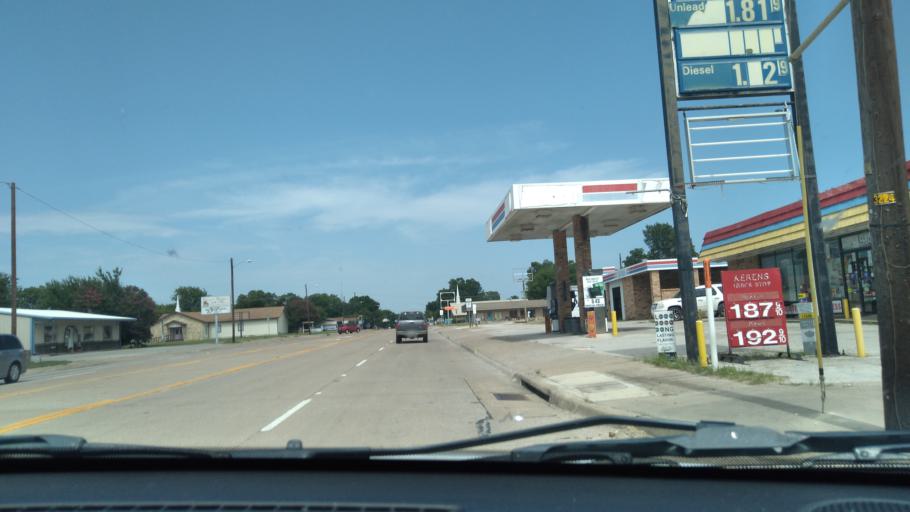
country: US
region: Texas
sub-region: Navarro County
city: Kerens
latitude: 32.1326
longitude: -96.2330
